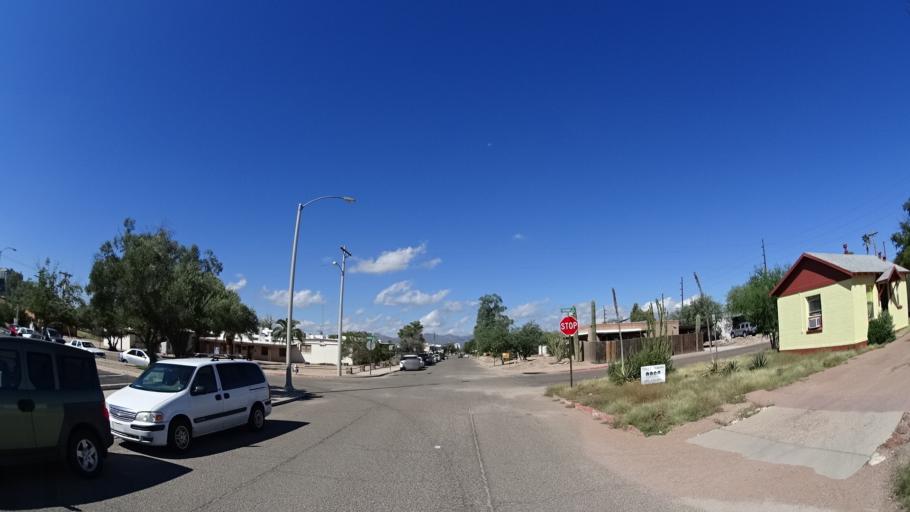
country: US
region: Arizona
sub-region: Pima County
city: Tucson
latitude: 32.2405
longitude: -110.9549
